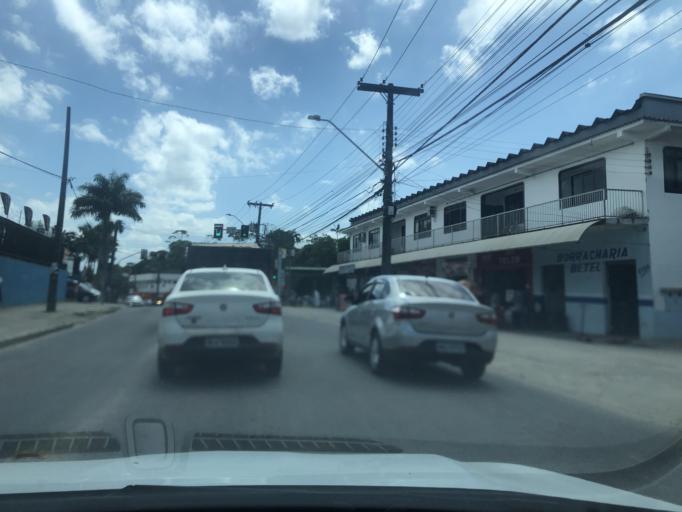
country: BR
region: Santa Catarina
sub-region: Joinville
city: Joinville
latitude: -26.3383
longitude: -48.8047
